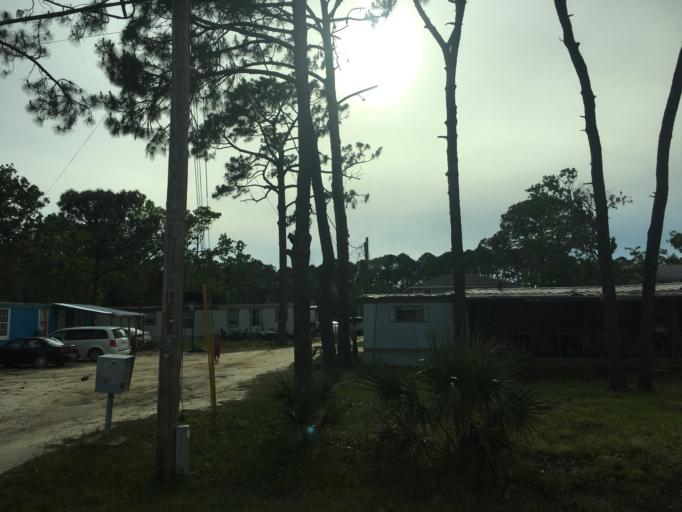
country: US
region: Florida
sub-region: Bay County
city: Panama City Beach
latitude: 30.1757
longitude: -85.7824
